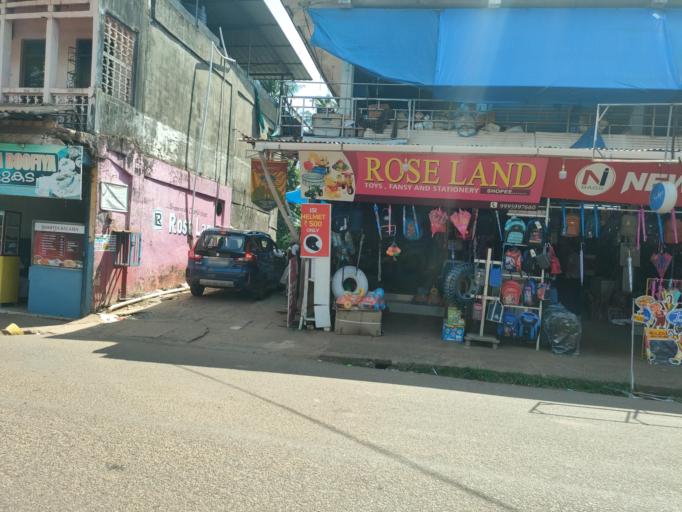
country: IN
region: Kerala
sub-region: Kasaragod District
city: Kasaragod
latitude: 12.4990
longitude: 74.9869
